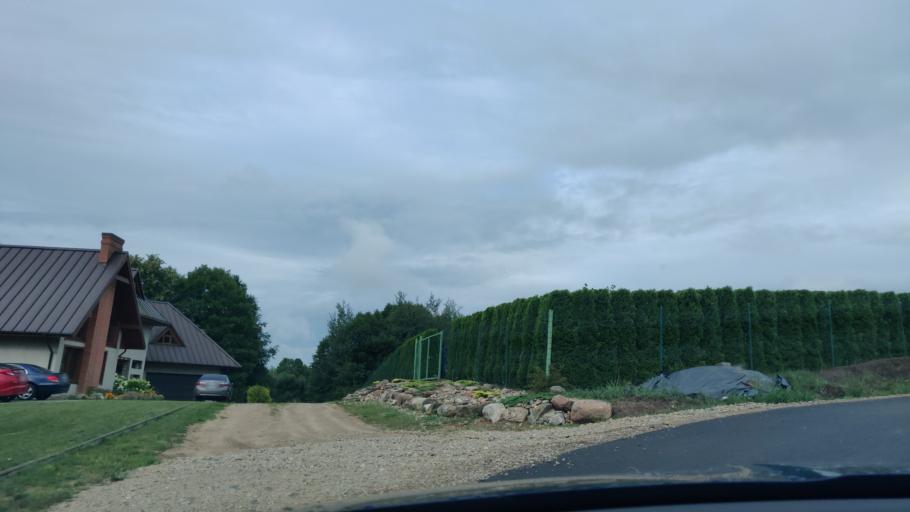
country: LT
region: Vilnius County
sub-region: Trakai
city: Rudiskes
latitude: 54.6099
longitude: 24.8193
